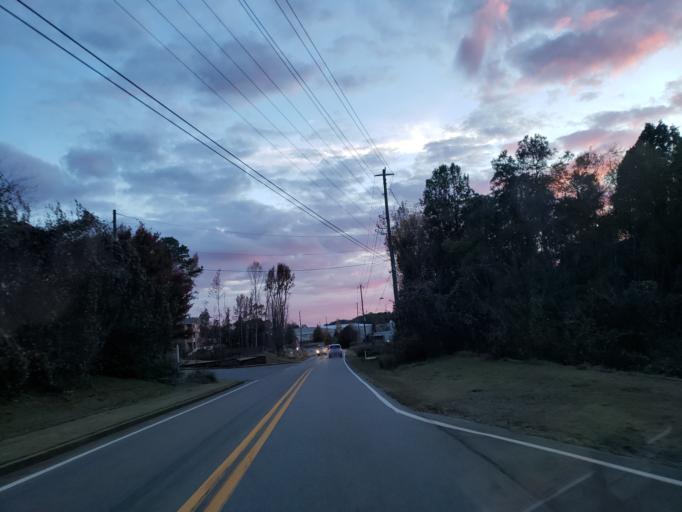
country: US
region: Georgia
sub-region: Bartow County
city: Cartersville
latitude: 34.1928
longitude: -84.7820
